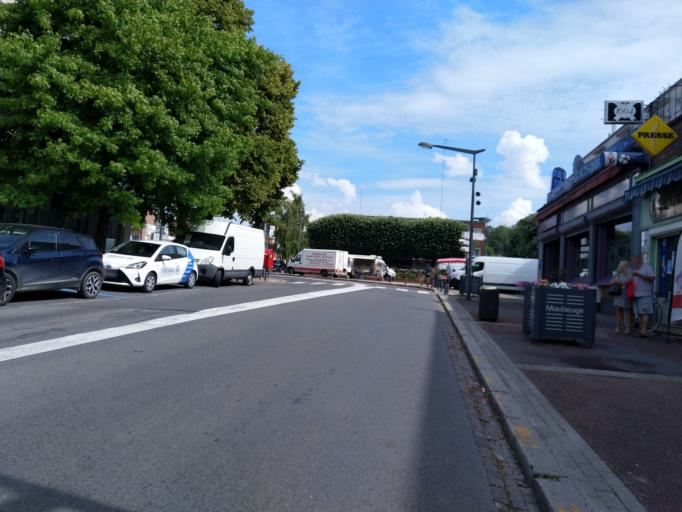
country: FR
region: Nord-Pas-de-Calais
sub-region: Departement du Nord
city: Maubeuge
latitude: 50.2780
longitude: 3.9743
